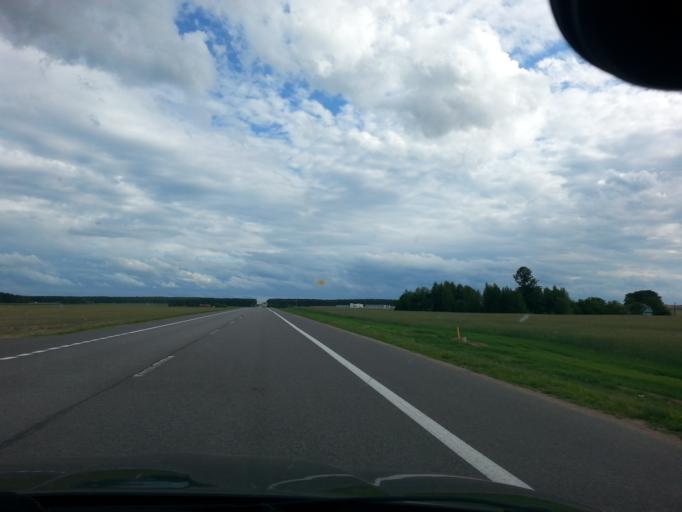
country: BY
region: Grodnenskaya
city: Astravyets
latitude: 54.7236
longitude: 26.0846
